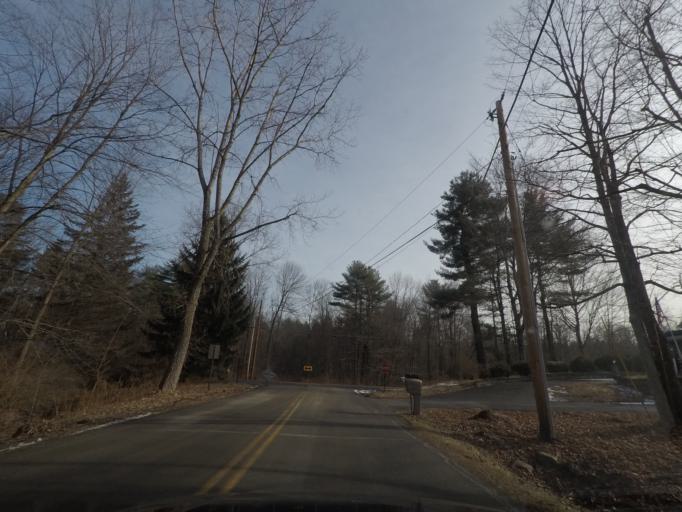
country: US
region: New York
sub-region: Saratoga County
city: Stillwater
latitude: 42.9888
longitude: -73.7151
